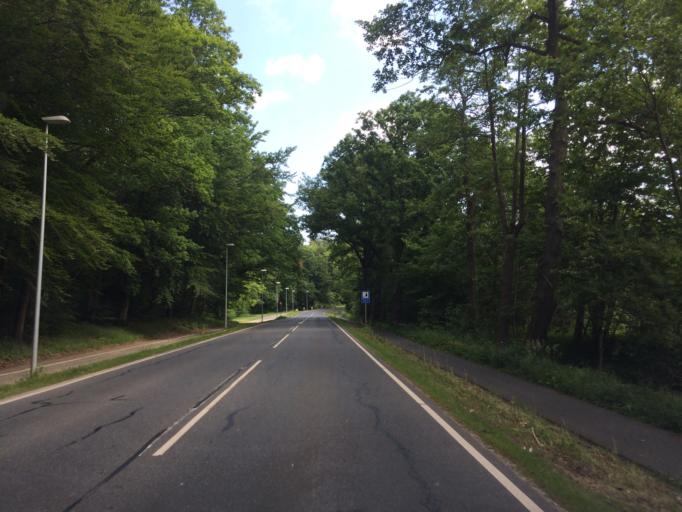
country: DK
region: Central Jutland
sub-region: Silkeborg Kommune
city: Silkeborg
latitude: 56.1608
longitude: 9.5181
